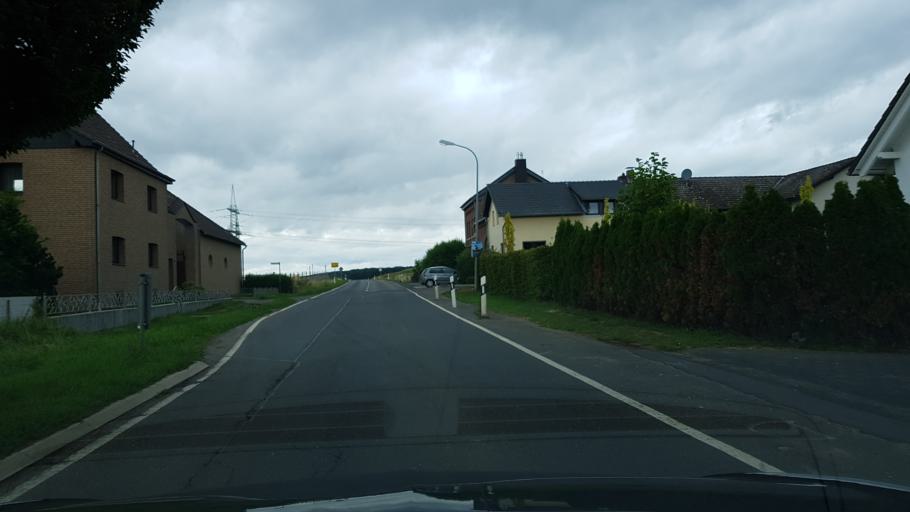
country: DE
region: North Rhine-Westphalia
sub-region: Regierungsbezirk Koln
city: Wachtberg
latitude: 50.6098
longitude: 7.0858
